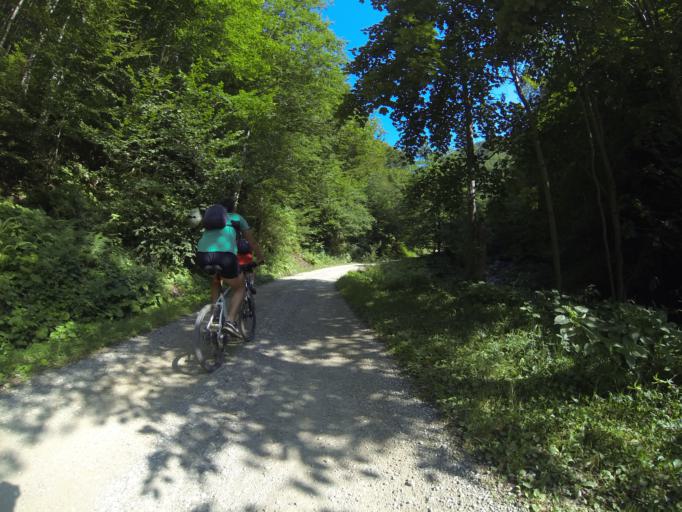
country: RO
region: Valcea
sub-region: Comuna Costesti
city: Bistrita
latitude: 45.2326
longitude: 24.0023
